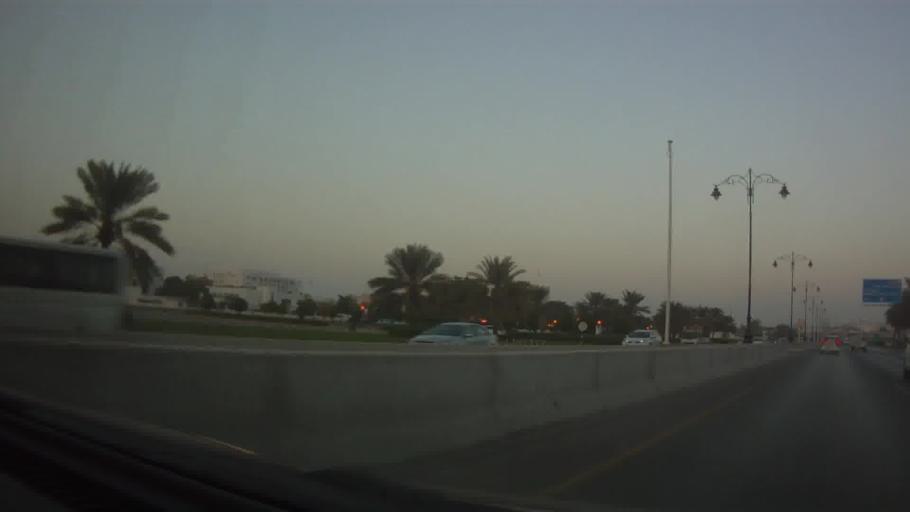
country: OM
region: Muhafazat Masqat
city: Bawshar
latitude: 23.5971
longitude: 58.4335
